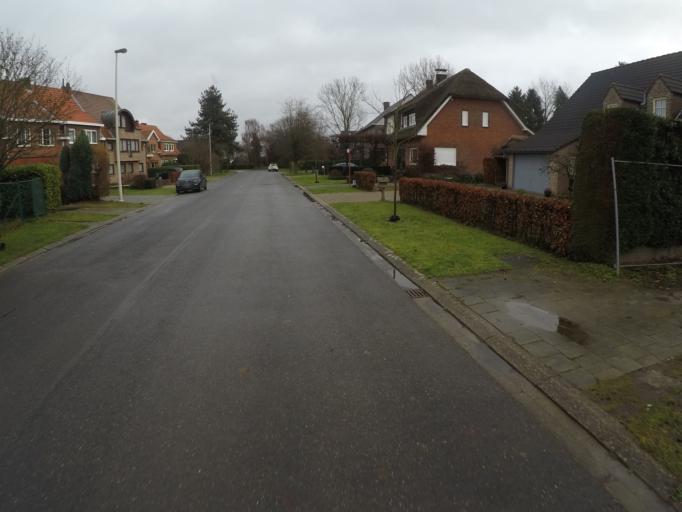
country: BE
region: Flanders
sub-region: Provincie Antwerpen
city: Wijnegem
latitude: 51.2209
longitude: 4.5093
